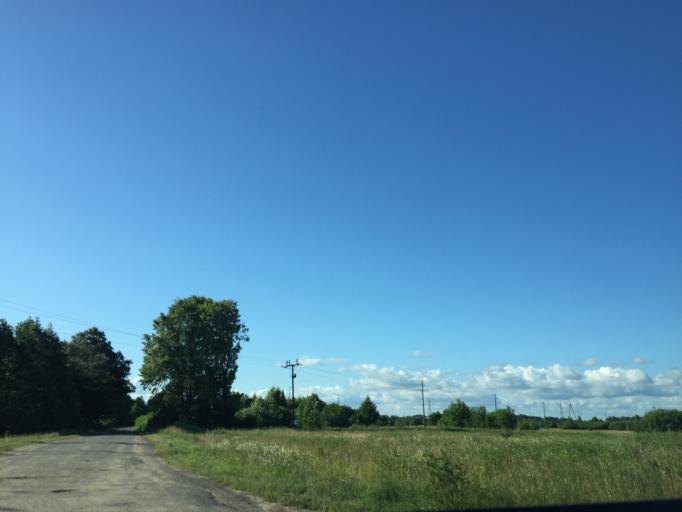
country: LV
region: Ventspils
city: Ventspils
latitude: 57.4083
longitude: 21.6450
